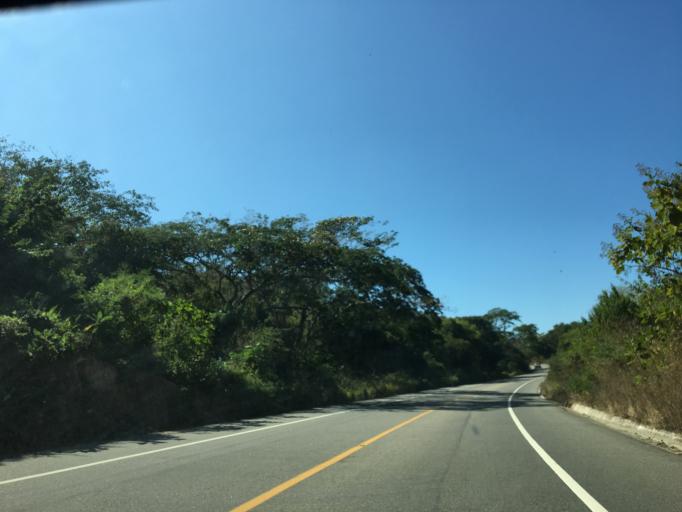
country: MX
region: Oaxaca
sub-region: Santa Maria Huatulco
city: Cuapinolito (Azulillo)
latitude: 15.7723
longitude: -96.2452
